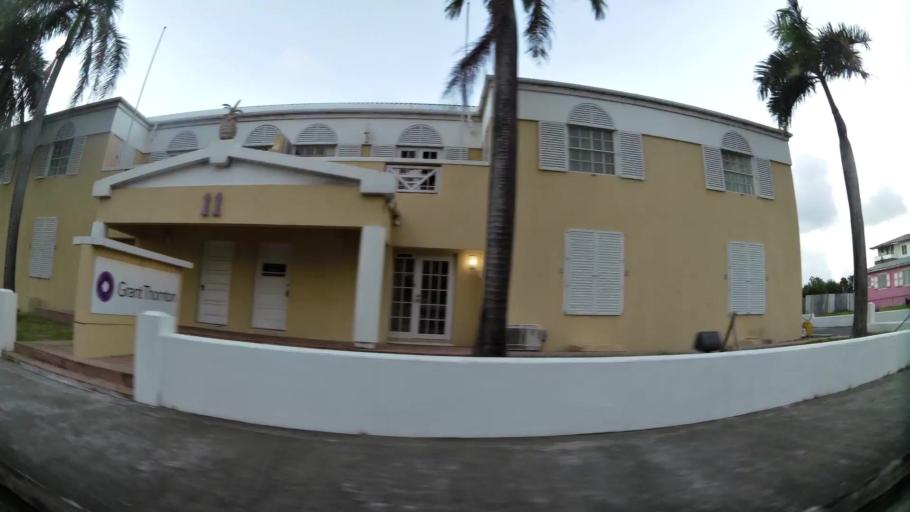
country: AG
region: Saint John
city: Saint John's
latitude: 17.1238
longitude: -61.8356
